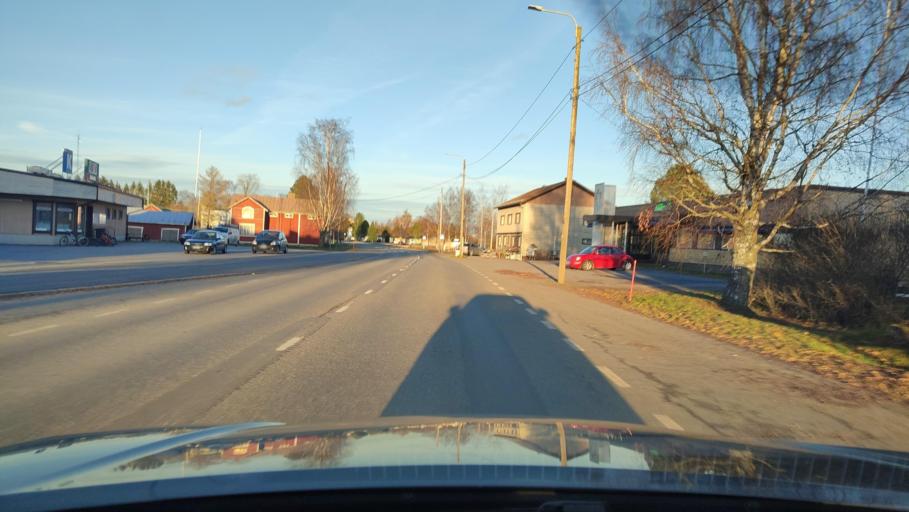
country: FI
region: Ostrobothnia
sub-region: Sydosterbotten
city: Naerpes
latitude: 62.6107
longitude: 21.4697
